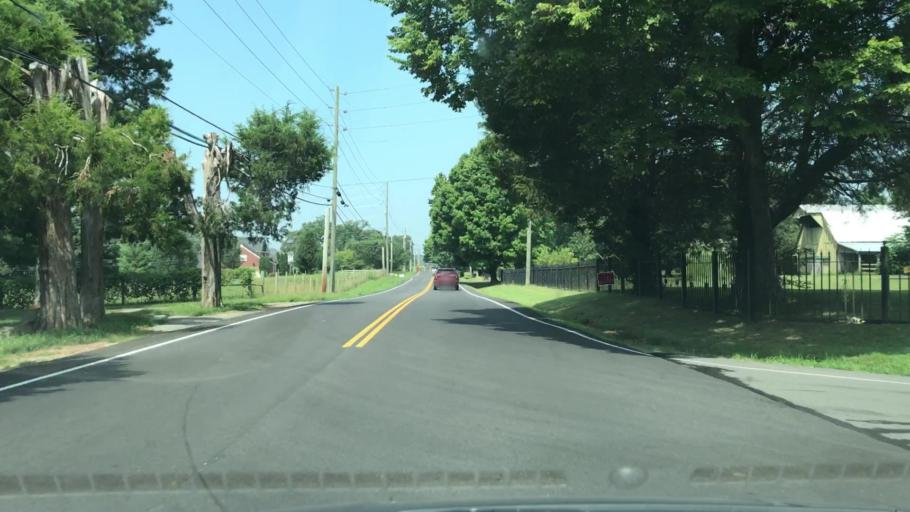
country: US
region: Tennessee
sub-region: Wilson County
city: Rural Hill
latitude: 36.1168
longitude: -86.4774
